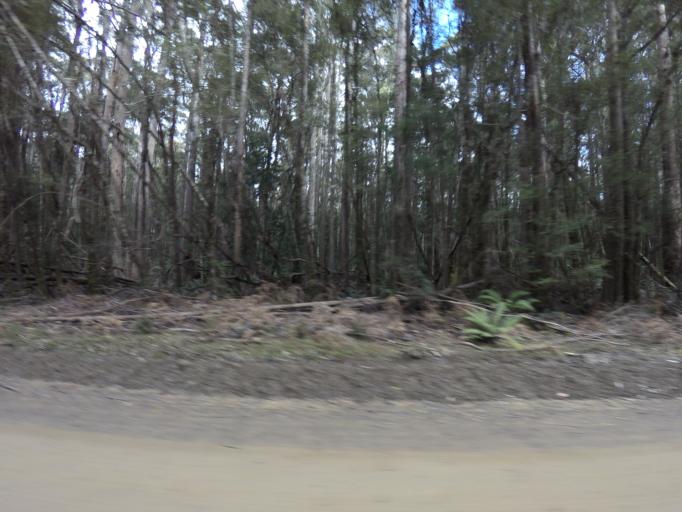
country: AU
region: Tasmania
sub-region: Huon Valley
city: Geeveston
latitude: -43.4027
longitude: 146.8647
